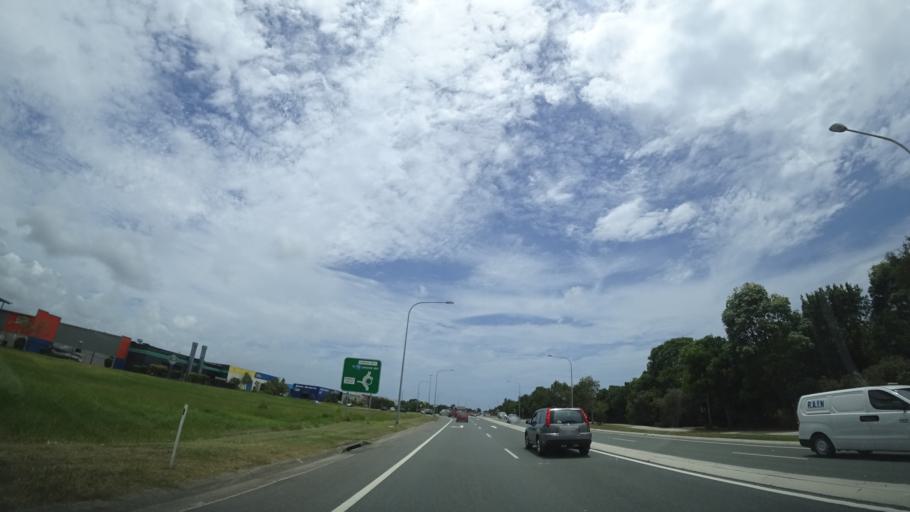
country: AU
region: Queensland
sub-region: Sunshine Coast
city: Mooloolaba
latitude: -26.7304
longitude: 153.1208
